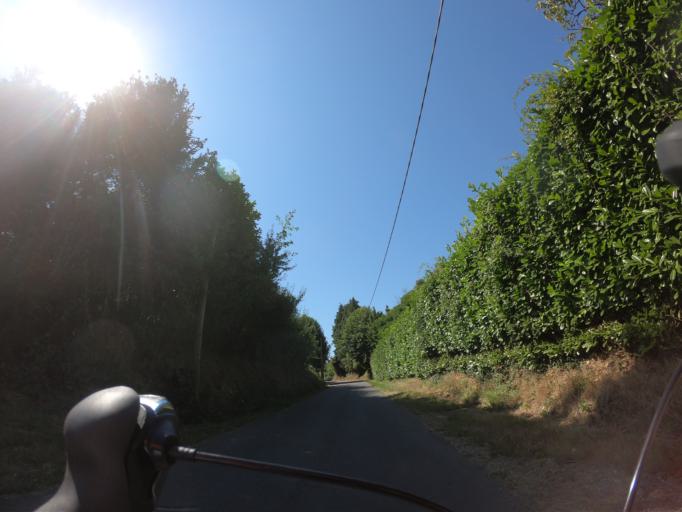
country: FR
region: Lower Normandy
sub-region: Departement de la Manche
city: Barenton
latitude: 48.5672
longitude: -0.7997
